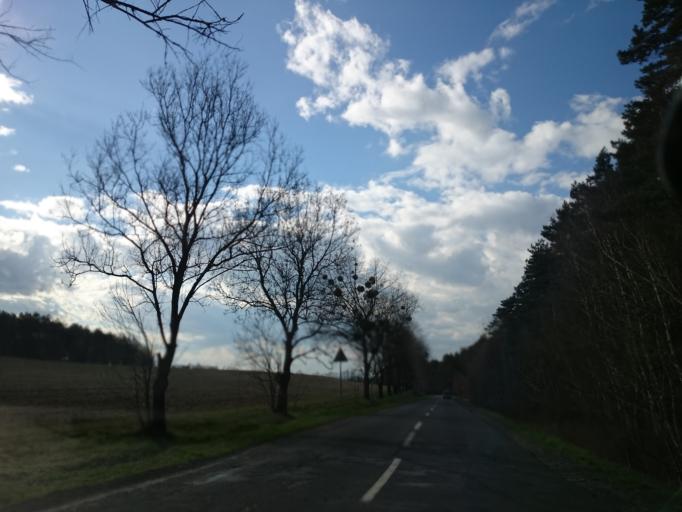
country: PL
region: Opole Voivodeship
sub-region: Powiat nyski
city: Sidzina
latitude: 50.6382
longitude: 17.5142
